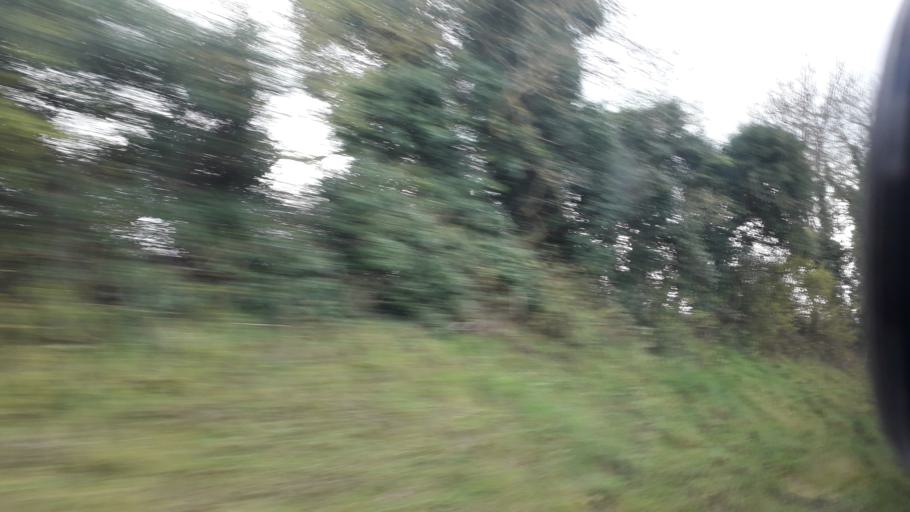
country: IE
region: Leinster
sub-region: An Iarmhi
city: Rathwire
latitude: 53.4902
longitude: -7.2027
